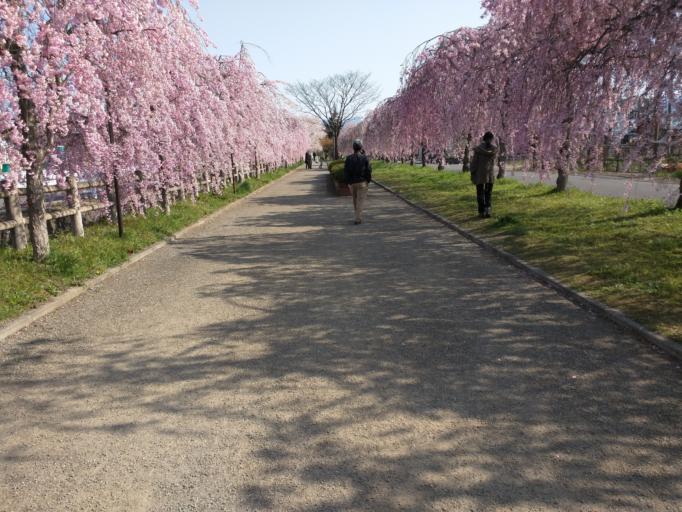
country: JP
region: Fukushima
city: Kitakata
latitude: 37.6588
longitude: 139.8682
